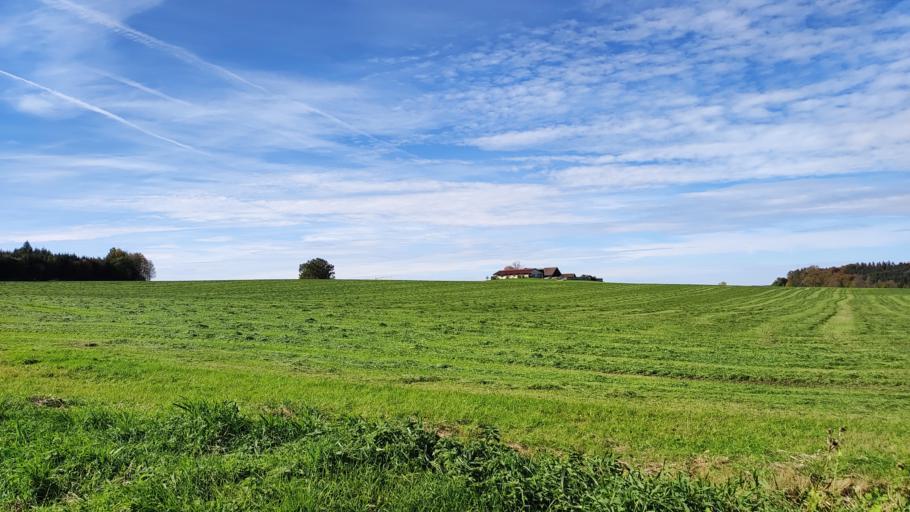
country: DE
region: Bavaria
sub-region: Swabia
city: Markt Rettenbach
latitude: 47.9850
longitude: 10.3928
